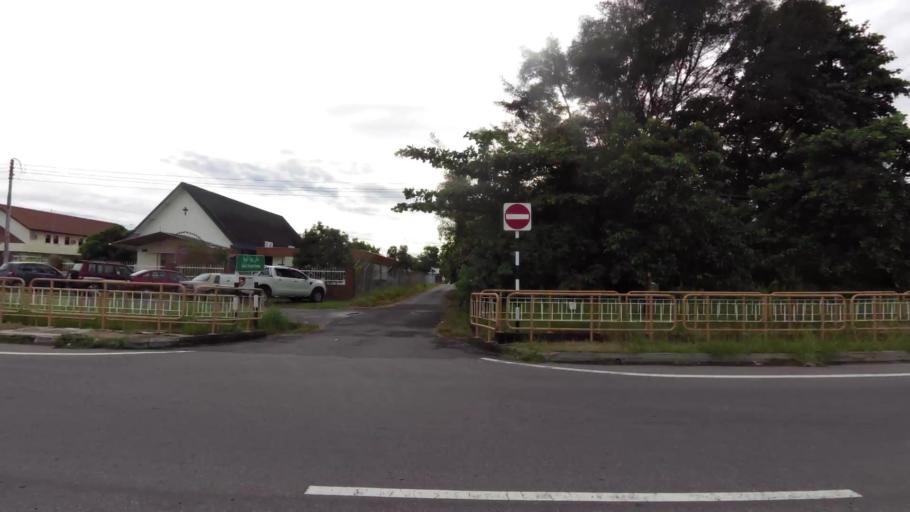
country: BN
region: Belait
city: Seria
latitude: 4.6123
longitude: 114.3268
